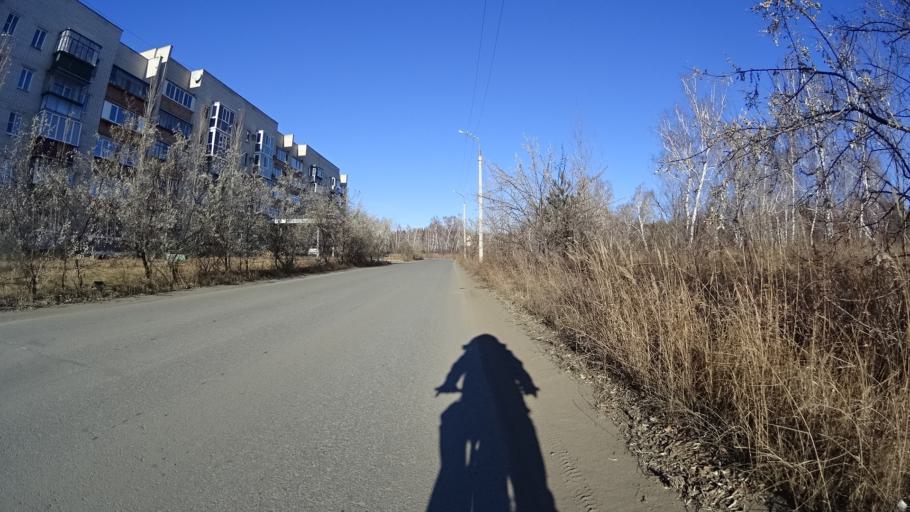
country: RU
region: Chelyabinsk
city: Troitsk
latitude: 54.0522
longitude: 61.6406
